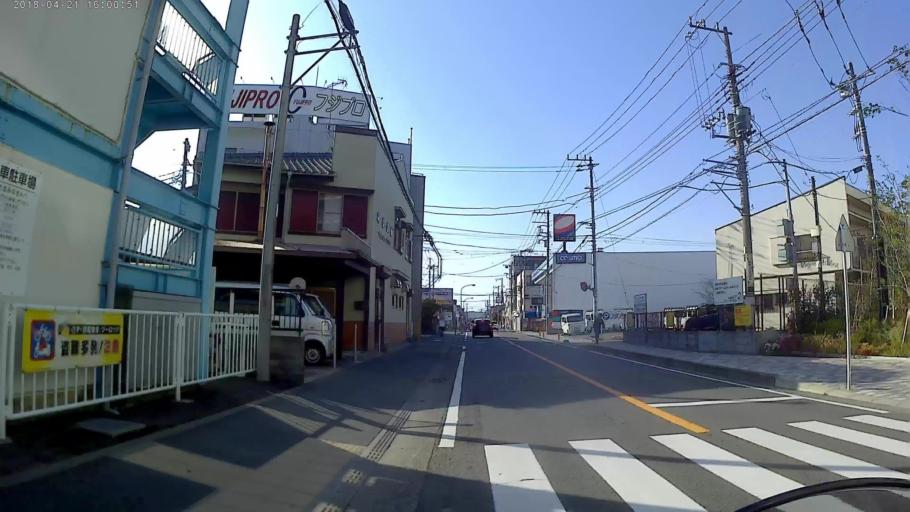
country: JP
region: Kanagawa
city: Fujisawa
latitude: 35.3387
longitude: 139.4410
